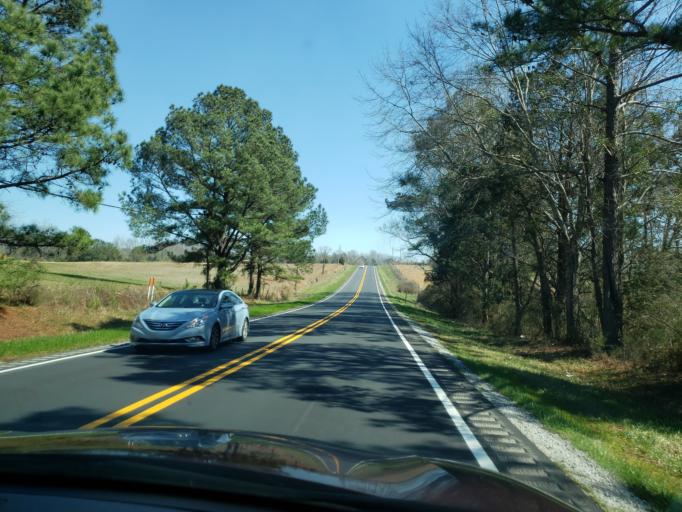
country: US
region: Alabama
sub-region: Macon County
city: Tuskegee
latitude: 32.5800
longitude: -85.7116
